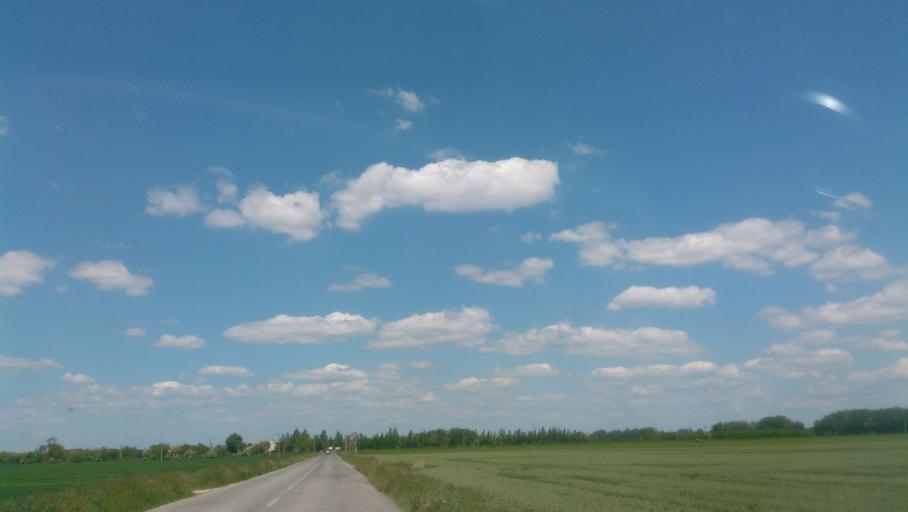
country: SK
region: Trnavsky
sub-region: Okres Dunajska Streda
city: Velky Meder
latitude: 47.9048
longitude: 17.8572
